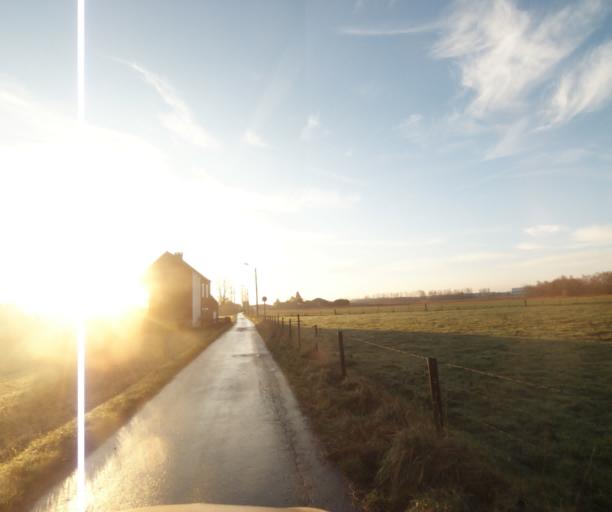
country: FR
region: Nord-Pas-de-Calais
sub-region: Departement du Nord
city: Quarouble
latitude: 50.3887
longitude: 3.6159
